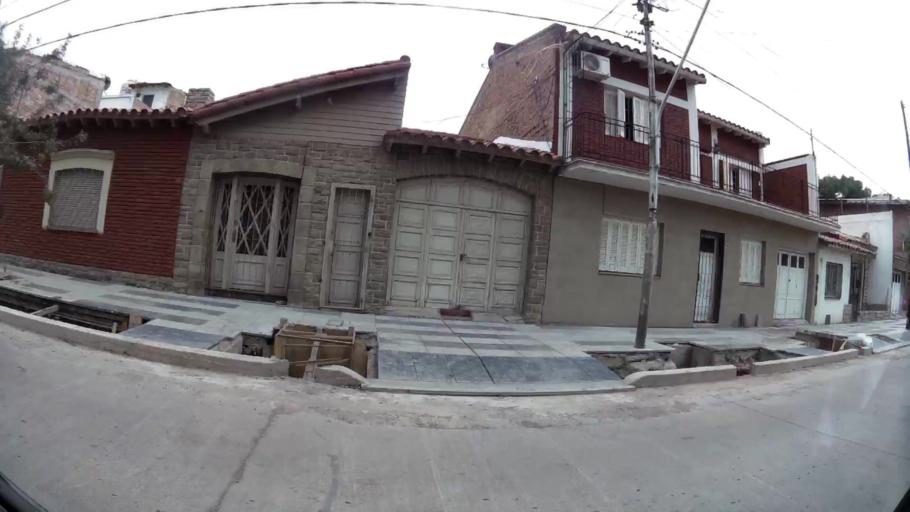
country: AR
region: Mendoza
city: Mendoza
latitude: -32.8826
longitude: -68.8301
